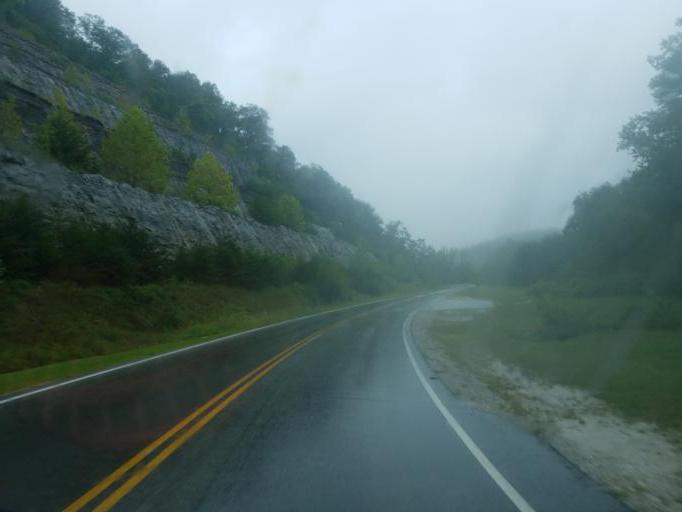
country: US
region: Kentucky
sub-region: Carter County
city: Grayson
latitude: 38.4682
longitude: -83.0493
